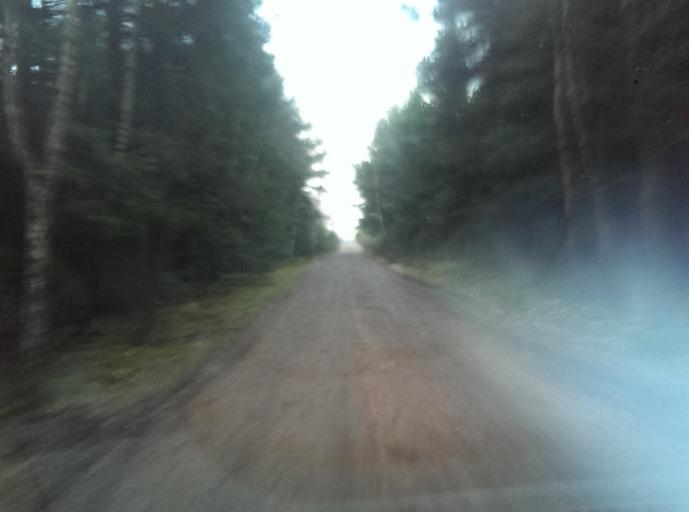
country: DK
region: South Denmark
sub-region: Varde Kommune
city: Oksbol
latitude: 55.5500
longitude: 8.3171
